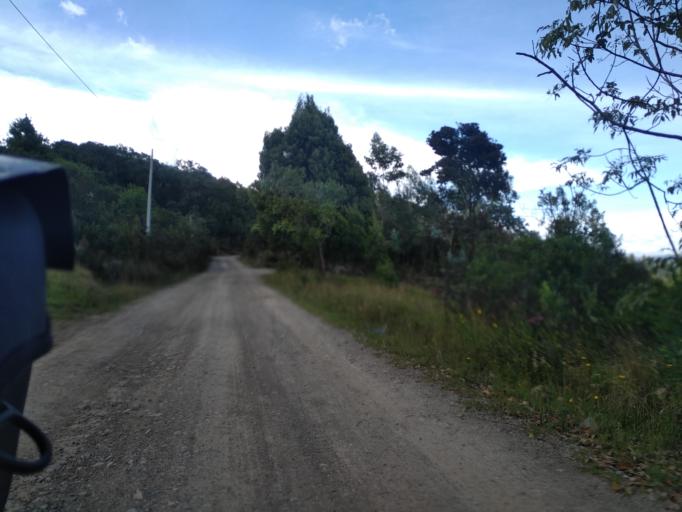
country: CO
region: Cundinamarca
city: Guacheta
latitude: 5.4506
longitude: -73.6521
